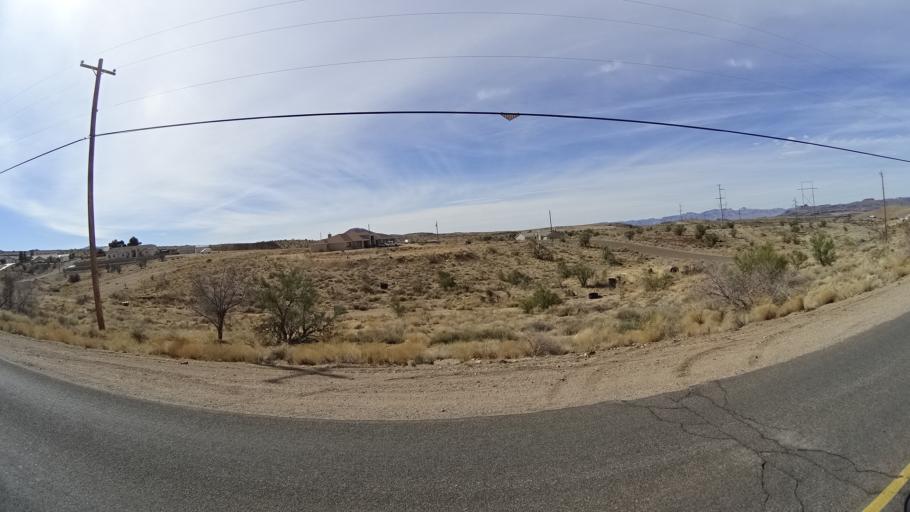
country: US
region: Arizona
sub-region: Mohave County
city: Kingman
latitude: 35.1741
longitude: -113.9856
